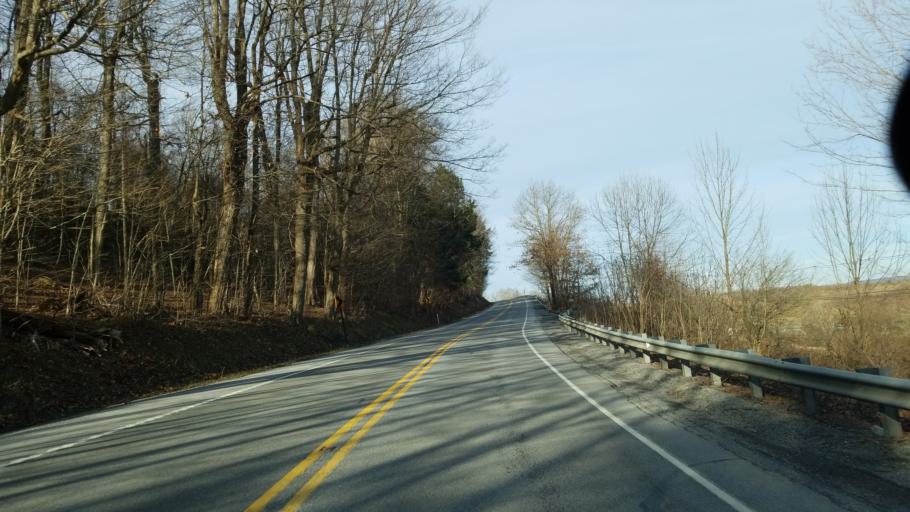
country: US
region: Pennsylvania
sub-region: Clearfield County
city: Curwensville
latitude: 40.9828
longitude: -78.6268
